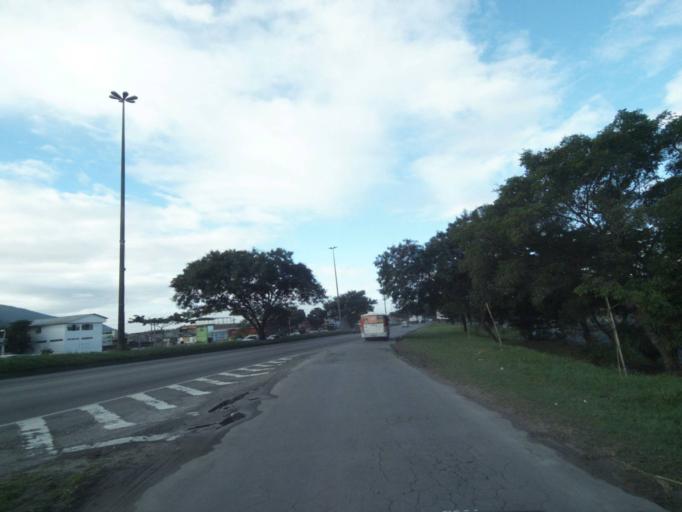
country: BR
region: Rio de Janeiro
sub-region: Nilopolis
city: Nilopolis
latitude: -22.8555
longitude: -43.4910
